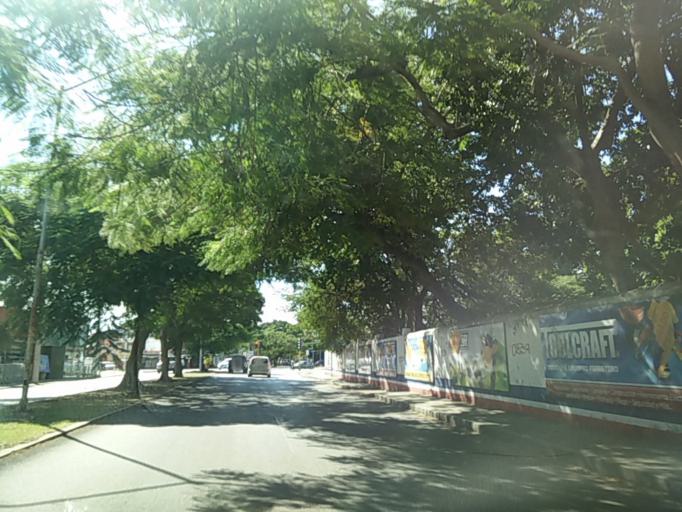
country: MX
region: Yucatan
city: Merida
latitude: 20.9903
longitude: -89.6063
